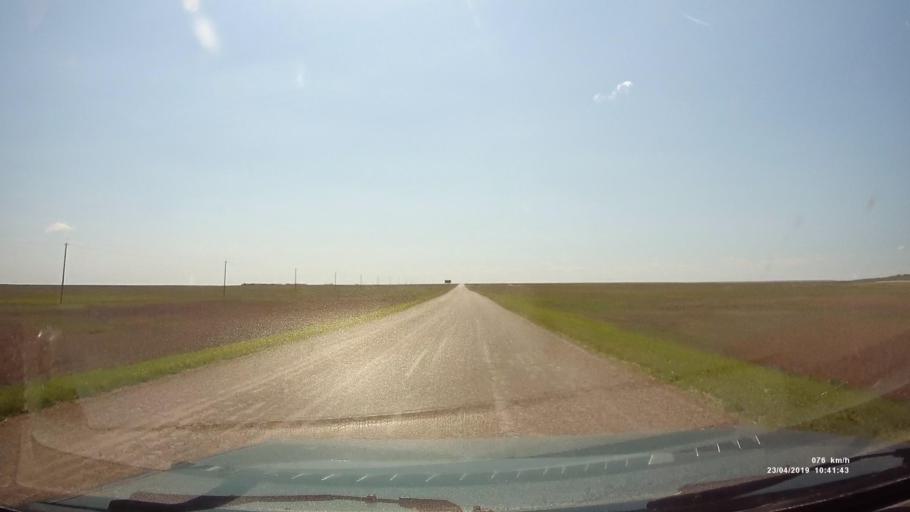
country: RU
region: Kalmykiya
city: Yashalta
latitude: 46.4909
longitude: 42.6387
